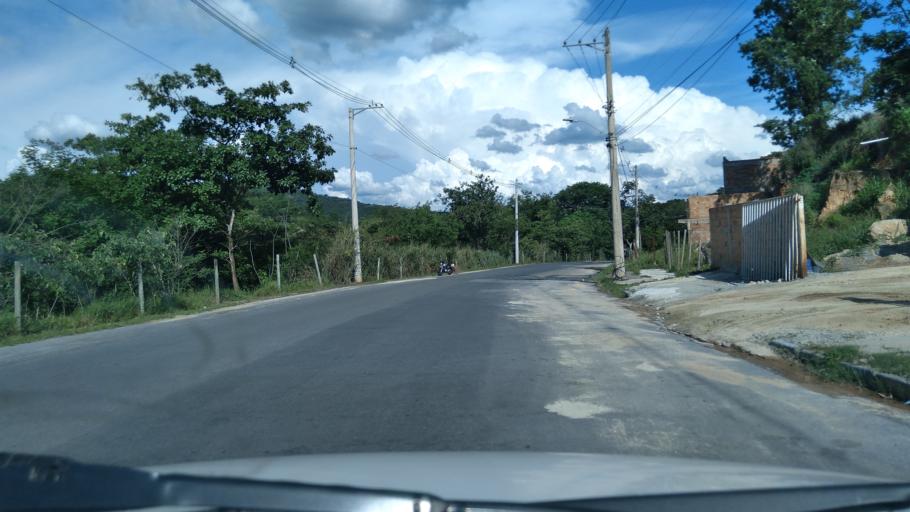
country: BR
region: Minas Gerais
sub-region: Santa Luzia
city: Santa Luzia
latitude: -19.8554
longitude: -43.8740
